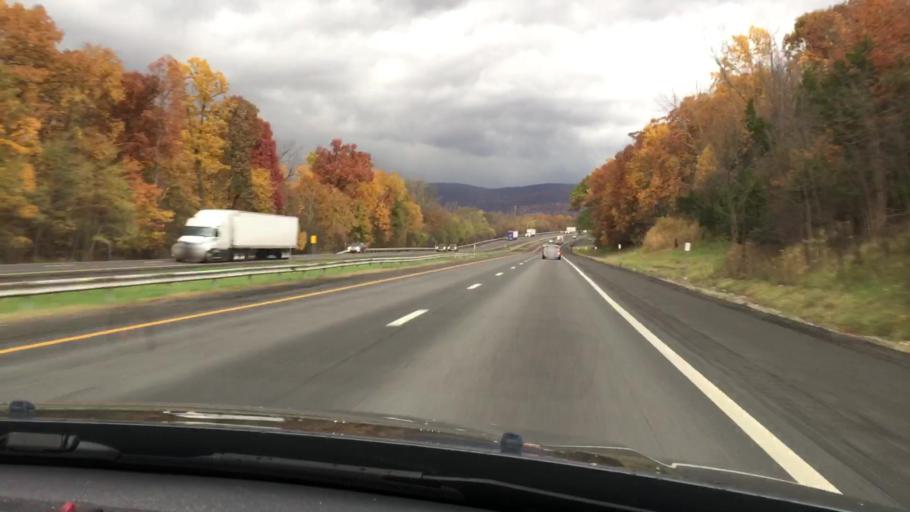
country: US
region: New York
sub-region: Orange County
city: Vails Gate
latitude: 41.4611
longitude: -74.0676
